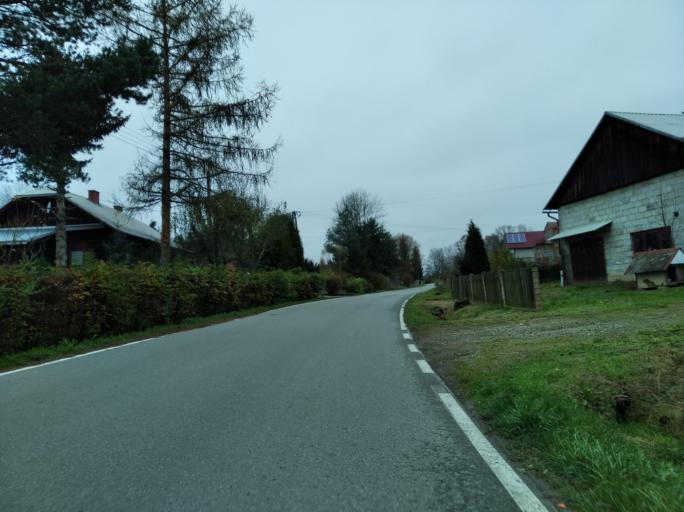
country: PL
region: Subcarpathian Voivodeship
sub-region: Powiat krosnienski
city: Leki
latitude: 49.8067
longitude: 21.6612
